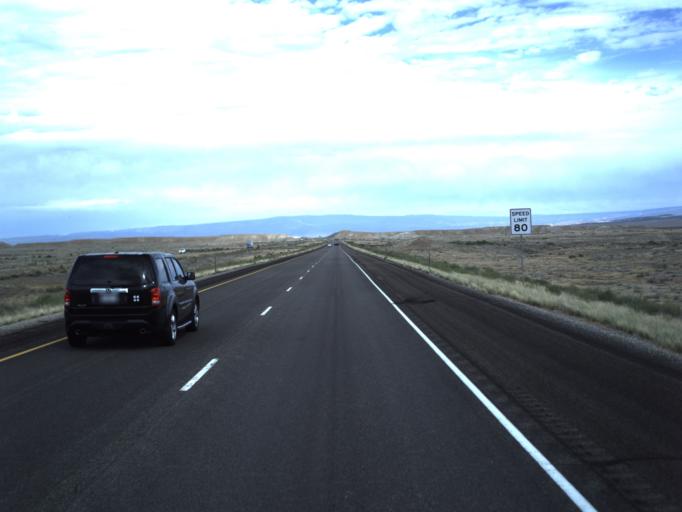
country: US
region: Utah
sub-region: Grand County
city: Moab
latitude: 38.9465
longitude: -109.6589
